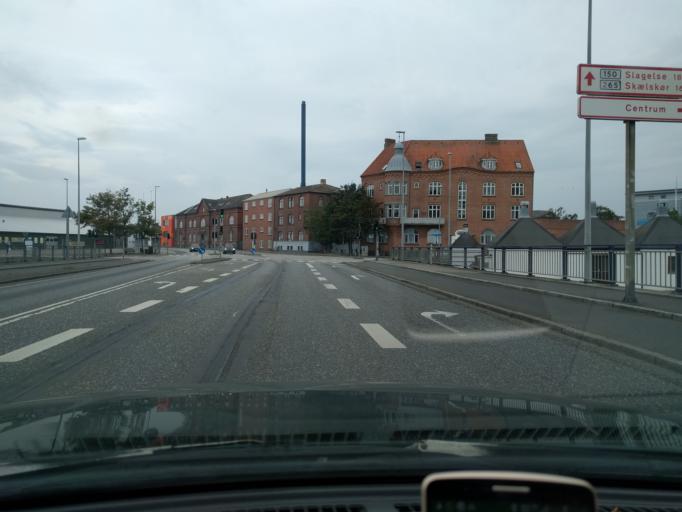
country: DK
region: Zealand
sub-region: Slagelse Kommune
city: Korsor
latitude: 55.3311
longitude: 11.1422
